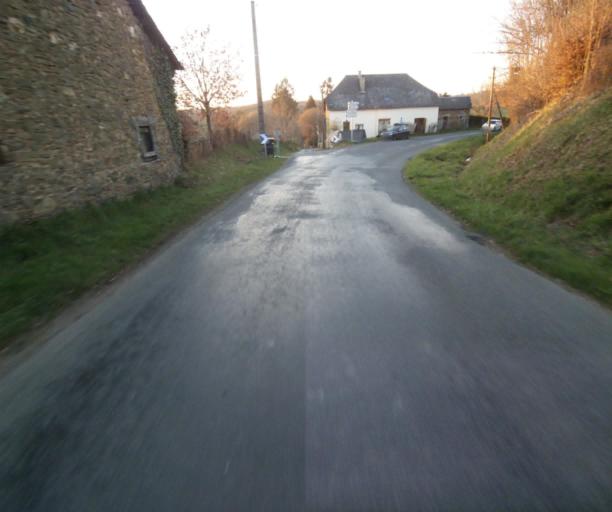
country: FR
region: Limousin
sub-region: Departement de la Correze
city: Saint-Clement
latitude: 45.3644
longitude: 1.6217
